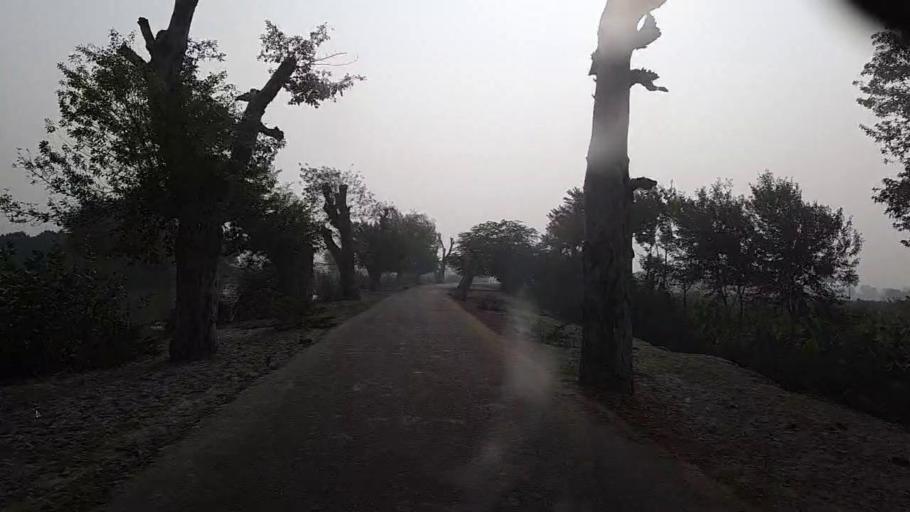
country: PK
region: Sindh
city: Bozdar
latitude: 27.1457
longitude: 68.6589
